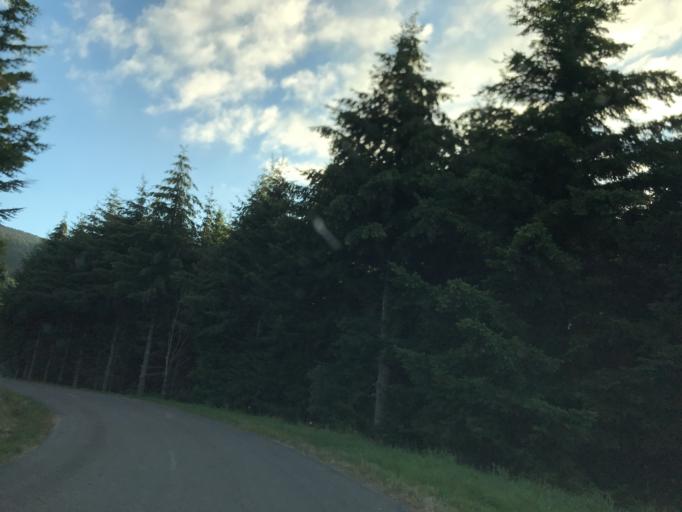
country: FR
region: Rhone-Alpes
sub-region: Departement de la Loire
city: Noiretable
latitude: 45.7858
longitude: 3.7831
